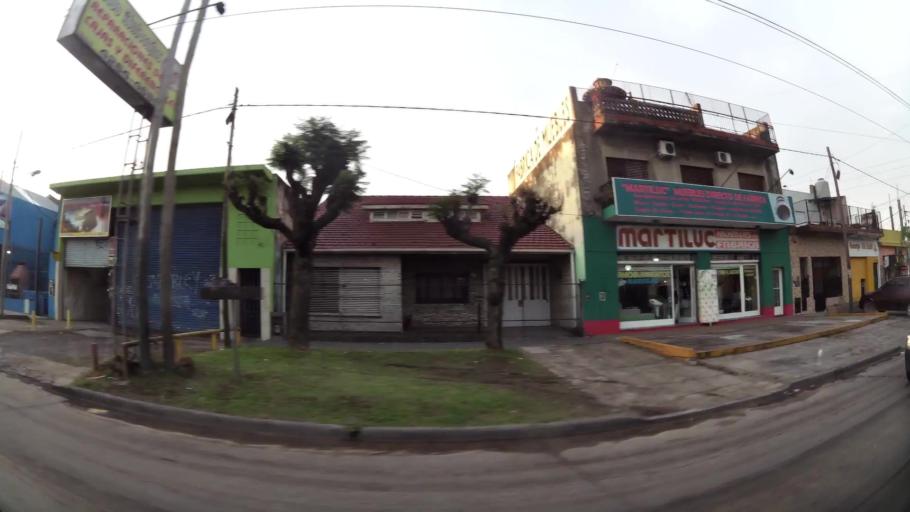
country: AR
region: Buenos Aires
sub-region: Partido de Lomas de Zamora
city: Lomas de Zamora
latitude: -34.7652
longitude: -58.3692
